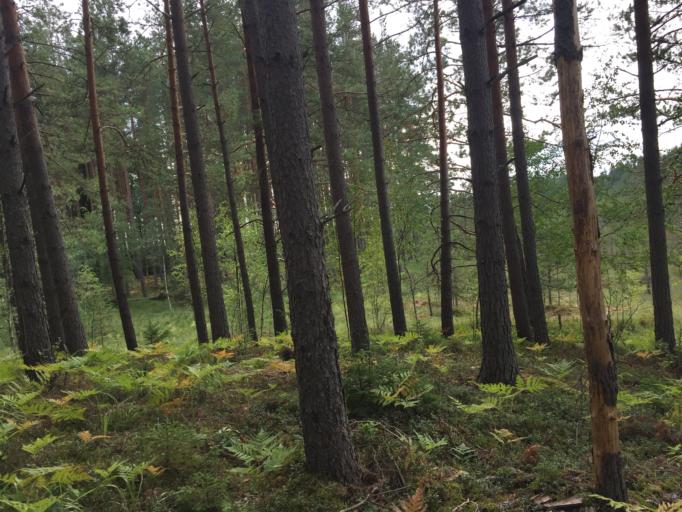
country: LV
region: Pargaujas
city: Stalbe
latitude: 57.3182
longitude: 25.0519
